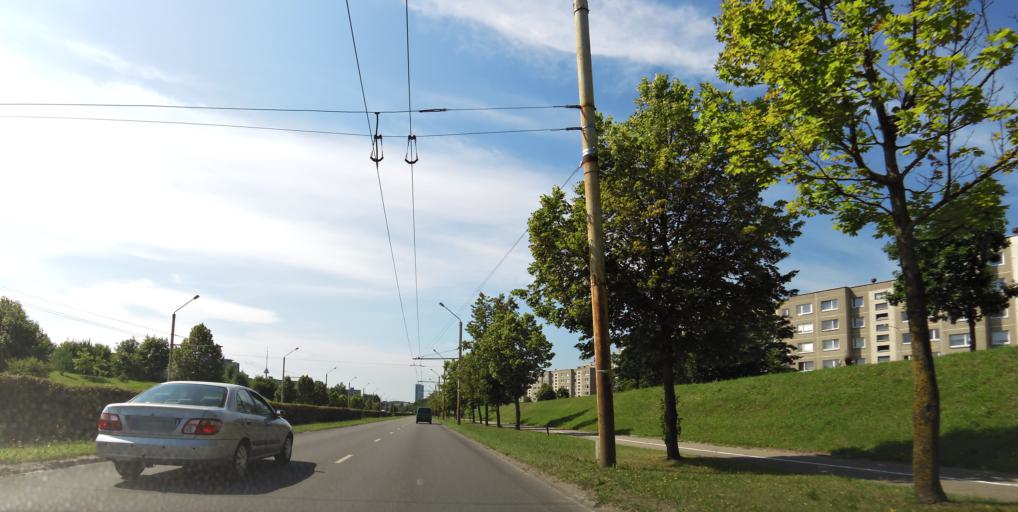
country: LT
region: Vilnius County
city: Justiniskes
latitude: 54.7159
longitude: 25.2205
